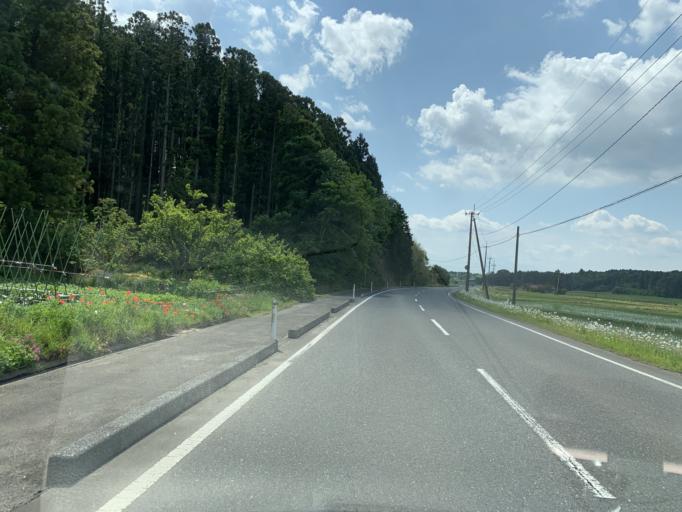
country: JP
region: Miyagi
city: Furukawa
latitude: 38.6844
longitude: 140.9742
